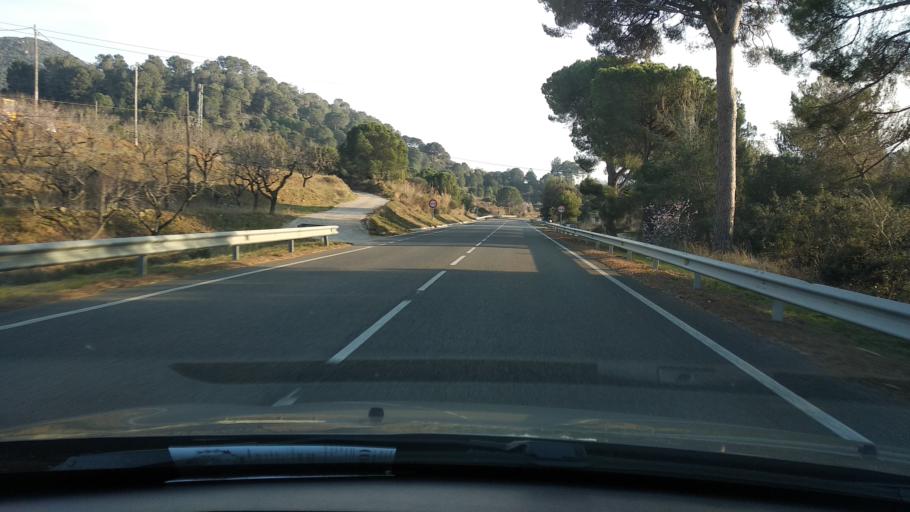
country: ES
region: Catalonia
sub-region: Provincia de Tarragona
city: Alforja
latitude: 41.1990
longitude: 0.9976
